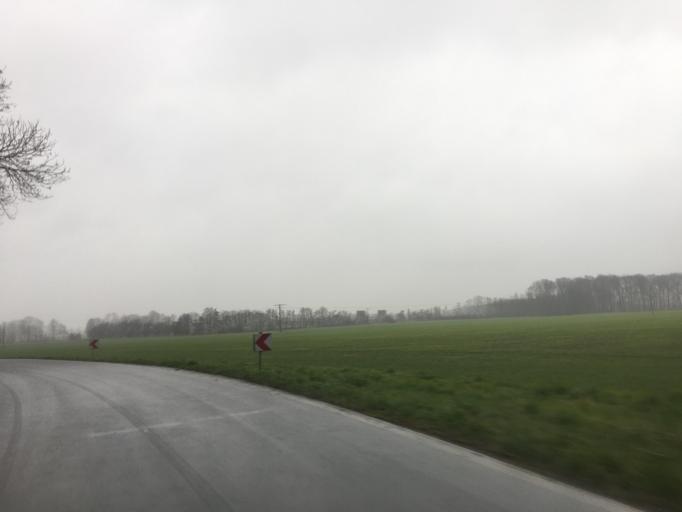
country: DE
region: North Rhine-Westphalia
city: Ludinghausen
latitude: 51.8161
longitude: 7.3762
